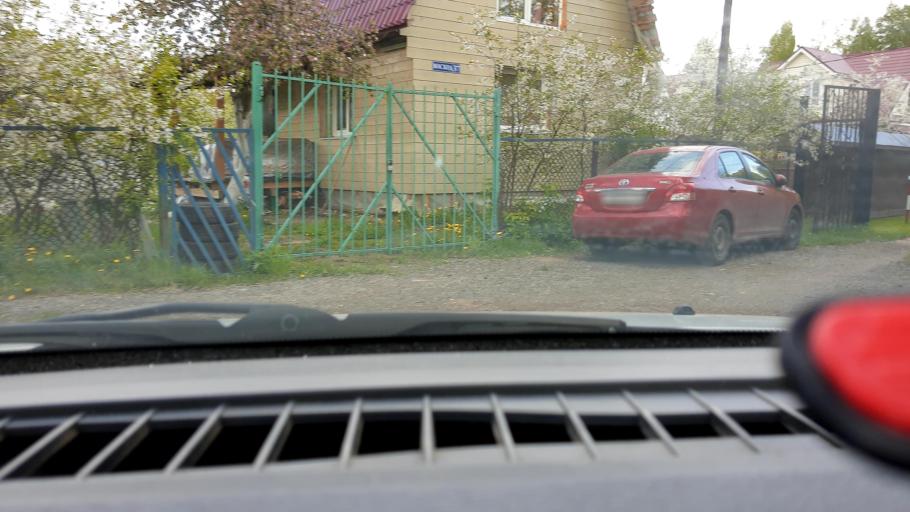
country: RU
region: Nizjnij Novgorod
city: Afonino
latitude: 56.2760
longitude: 44.0809
